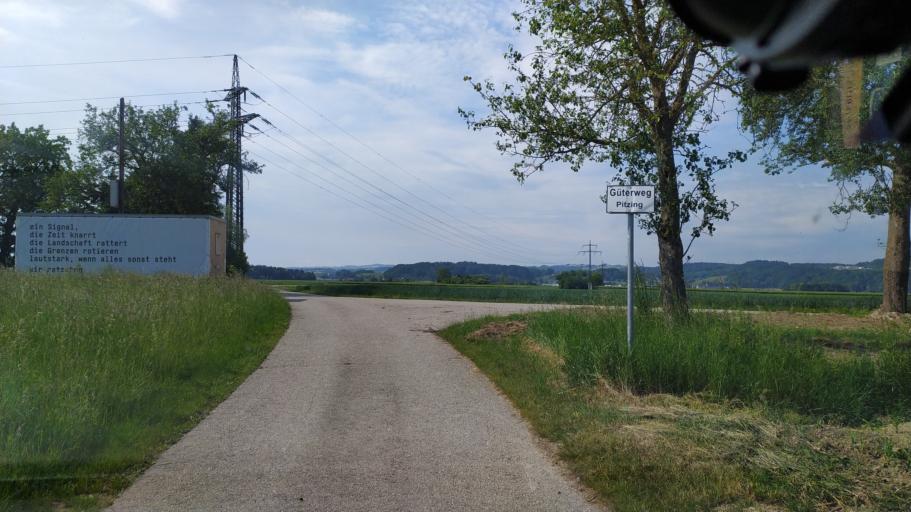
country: AT
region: Lower Austria
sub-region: Politischer Bezirk Amstetten
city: Zeillern
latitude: 48.1907
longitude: 14.7606
